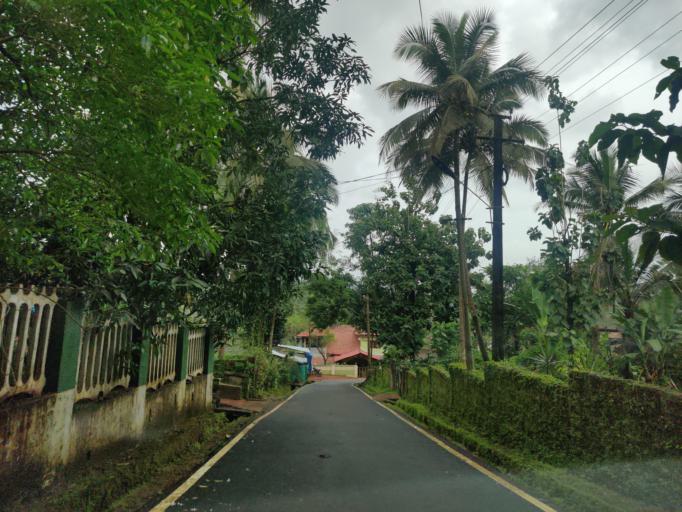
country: IN
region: Goa
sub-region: North Goa
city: Valpoy
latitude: 15.5274
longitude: 74.1412
